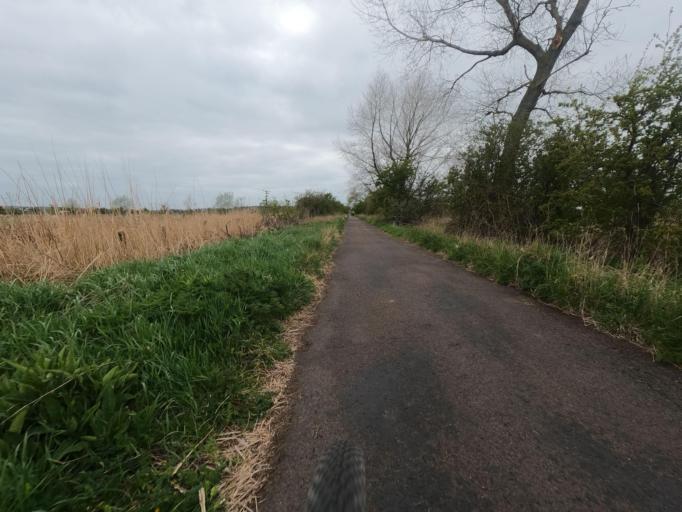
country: GB
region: England
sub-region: Newcastle upon Tyne
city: Dinnington
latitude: 55.0565
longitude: -1.7085
